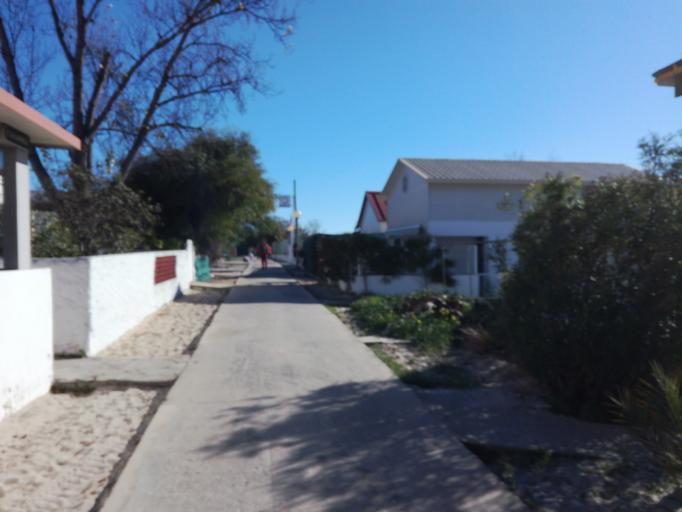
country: PT
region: Faro
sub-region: Olhao
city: Olhao
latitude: 37.0214
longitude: -7.8053
